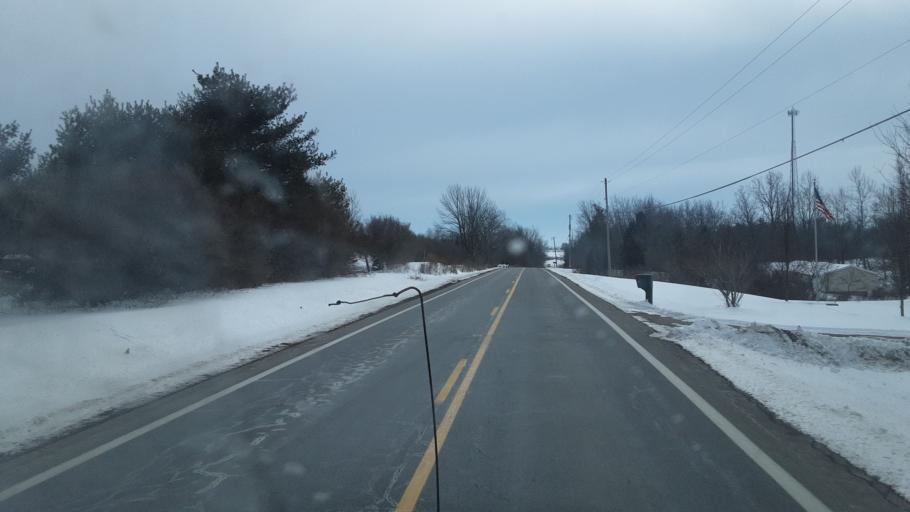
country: US
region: Ohio
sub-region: Madison County
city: Choctaw Lake
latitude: 39.9520
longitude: -83.5045
